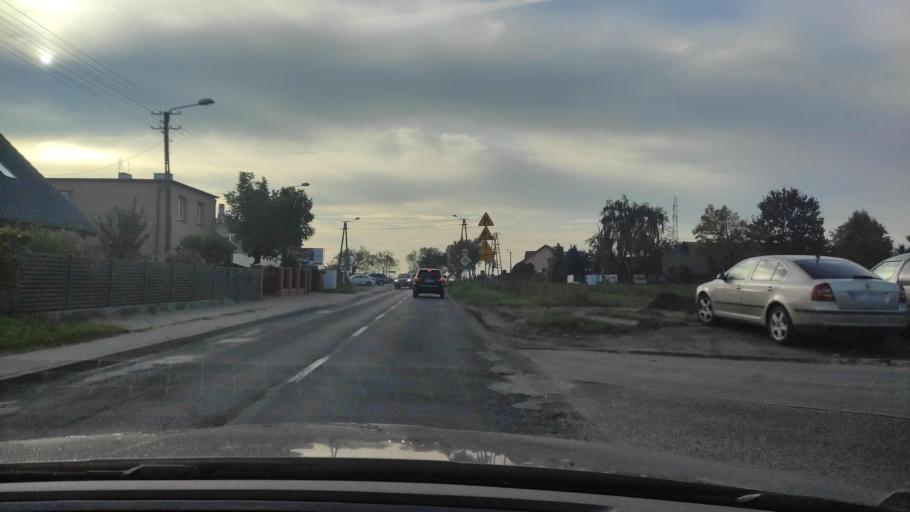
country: PL
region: Greater Poland Voivodeship
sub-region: Powiat poznanski
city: Kleszczewo
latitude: 52.3792
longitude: 17.1654
